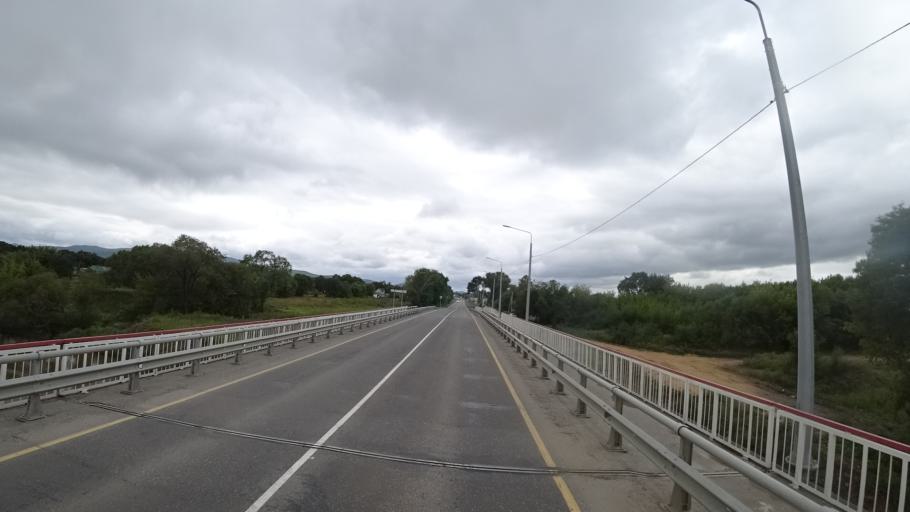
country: RU
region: Primorskiy
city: Chernigovka
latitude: 44.3425
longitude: 132.5906
